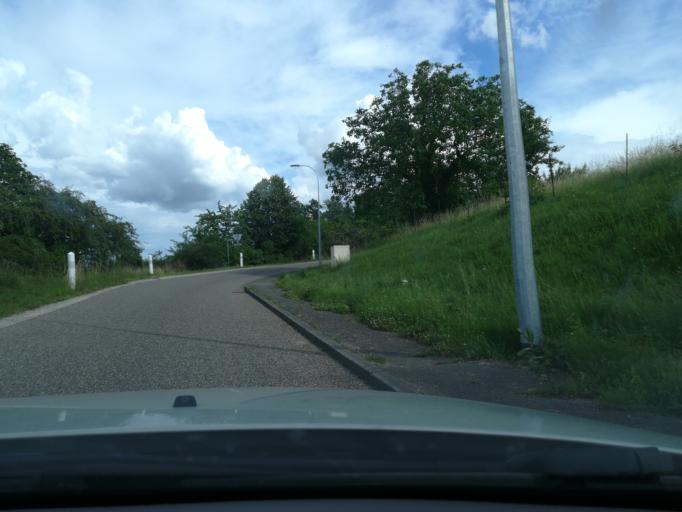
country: FR
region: Alsace
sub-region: Departement du Bas-Rhin
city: Ingwiller
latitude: 48.8638
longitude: 7.4821
